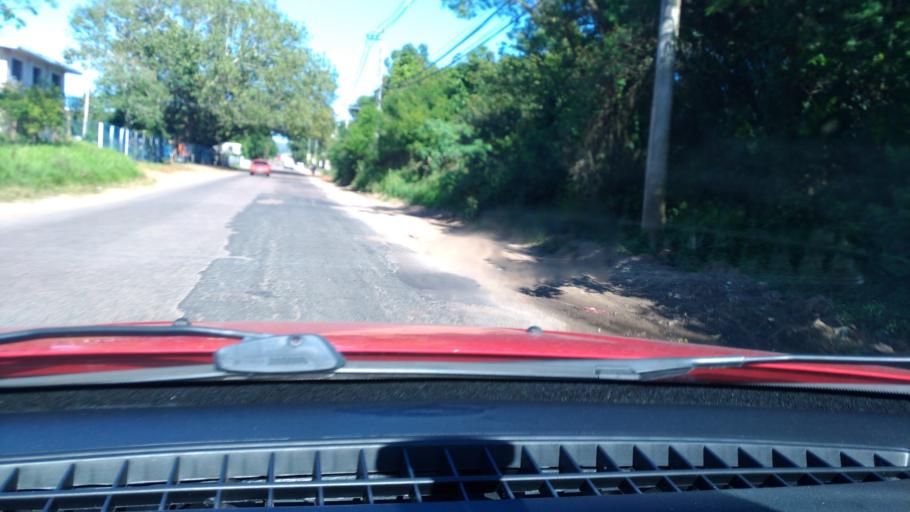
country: BR
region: Rio Grande do Sul
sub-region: Viamao
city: Viamao
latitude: -30.0501
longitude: -51.0639
